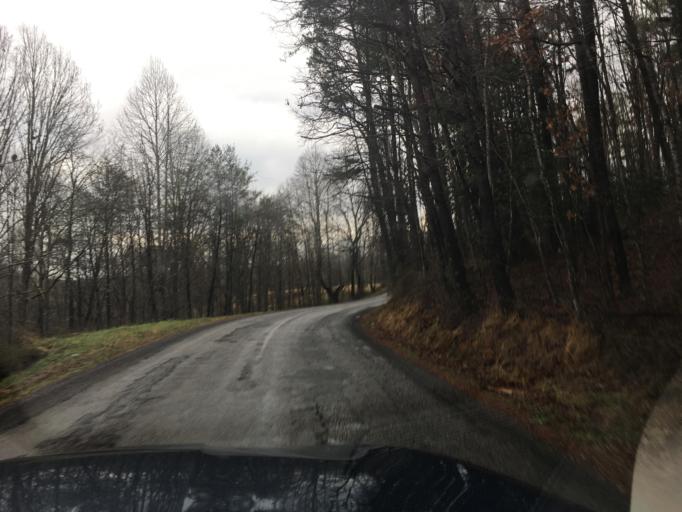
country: US
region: Georgia
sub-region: Fannin County
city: McCaysville
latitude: 35.1251
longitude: -84.3120
